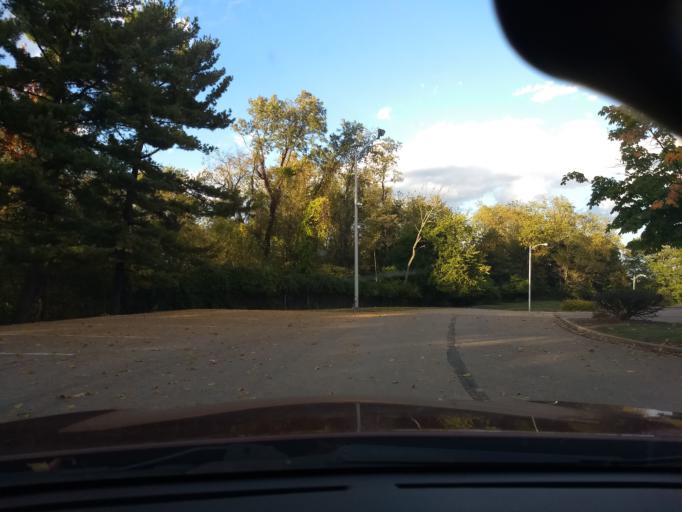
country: US
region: Pennsylvania
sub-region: Allegheny County
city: Dravosburg
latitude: 40.3581
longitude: -79.9045
